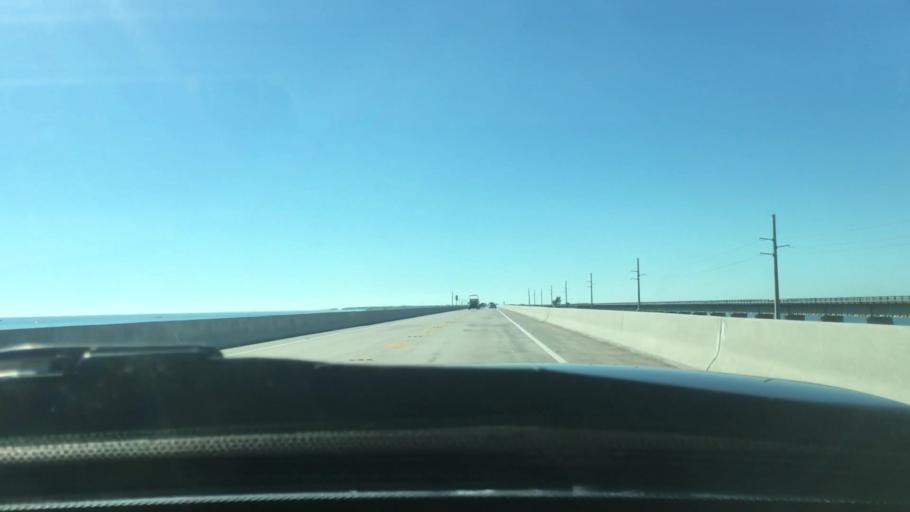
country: US
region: Florida
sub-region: Monroe County
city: Marathon
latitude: 24.6915
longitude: -81.1958
